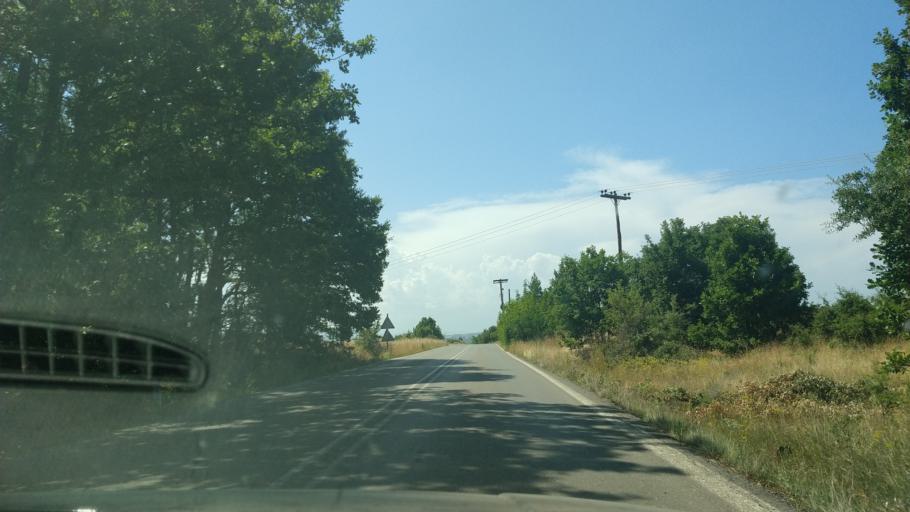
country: GR
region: West Macedonia
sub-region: Nomos Grevenon
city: Grevena
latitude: 40.0677
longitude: 21.4606
